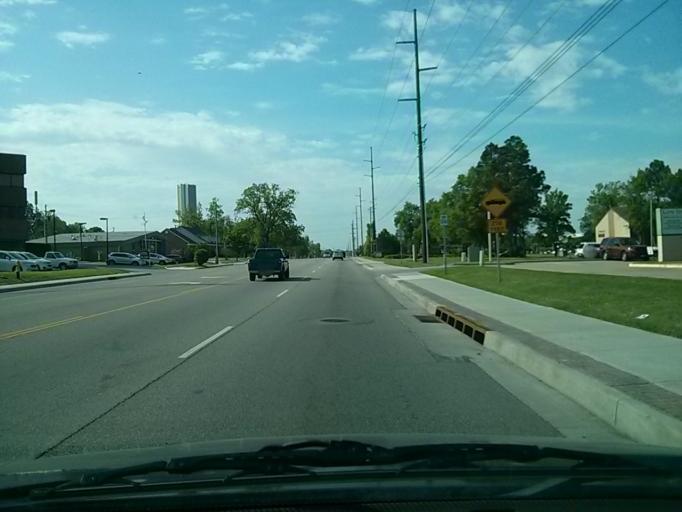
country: US
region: Oklahoma
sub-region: Tulsa County
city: Jenks
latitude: 36.0576
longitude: -95.9579
